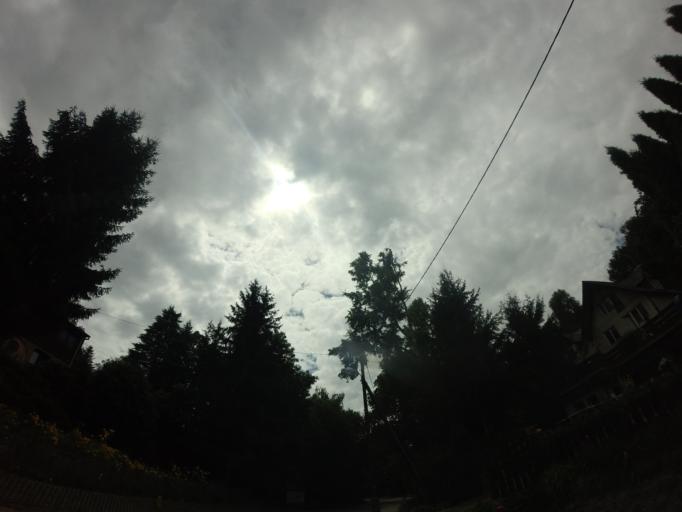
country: PL
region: Lublin Voivodeship
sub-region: Powiat pulawski
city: Kazimierz Dolny
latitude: 51.3108
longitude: 21.9503
